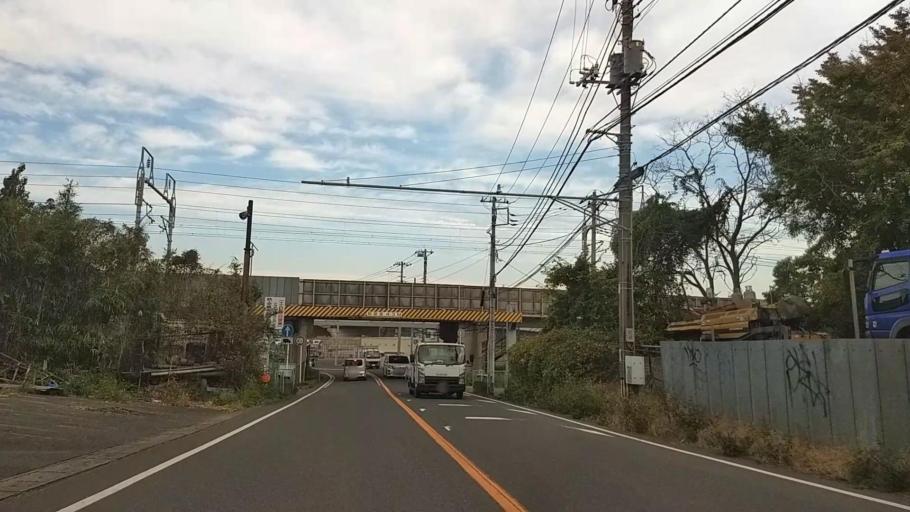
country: JP
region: Kanagawa
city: Atsugi
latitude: 35.4057
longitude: 139.4091
